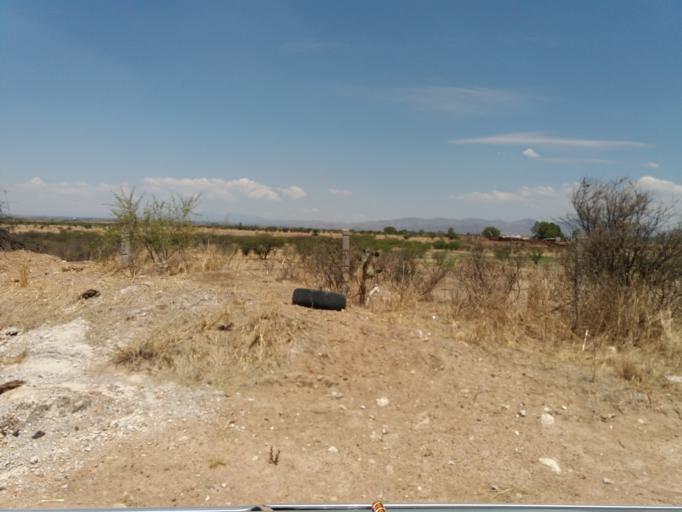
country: MX
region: Aguascalientes
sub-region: Aguascalientes
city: San Sebastian [Fraccionamiento]
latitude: 21.7967
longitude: -102.2981
